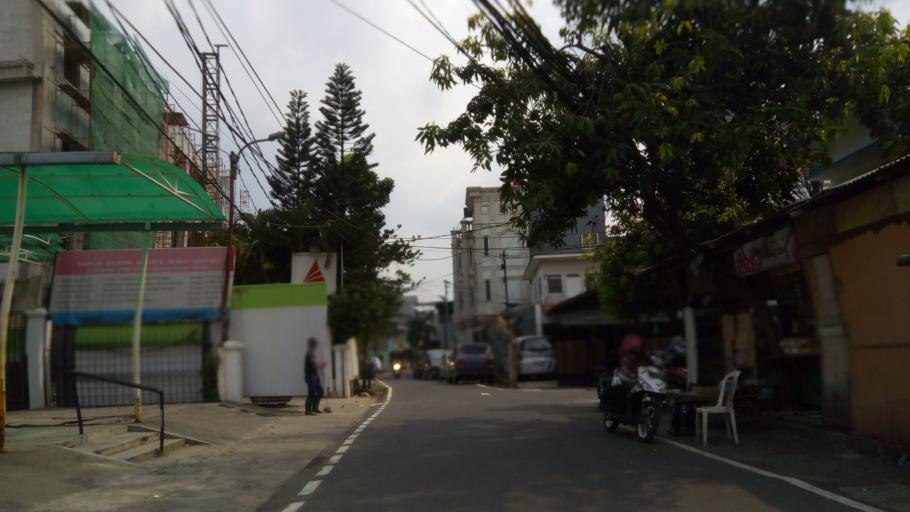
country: ID
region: Jakarta Raya
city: Jakarta
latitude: -6.1547
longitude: 106.8335
